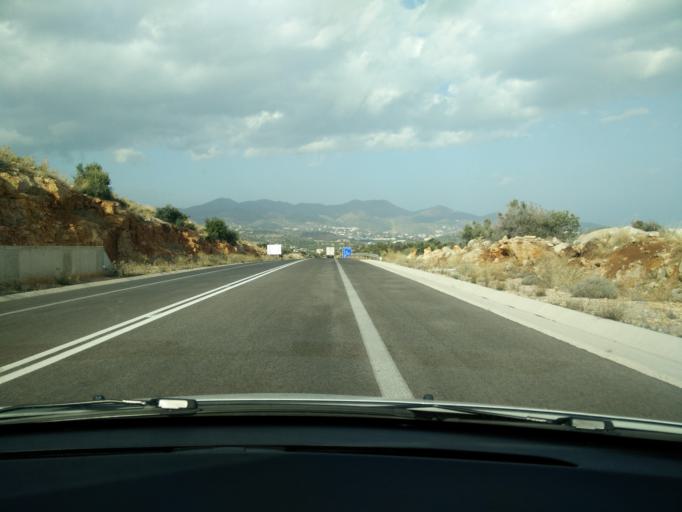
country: GR
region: Crete
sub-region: Nomos Lasithiou
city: Agios Nikolaos
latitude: 35.1745
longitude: 25.7008
